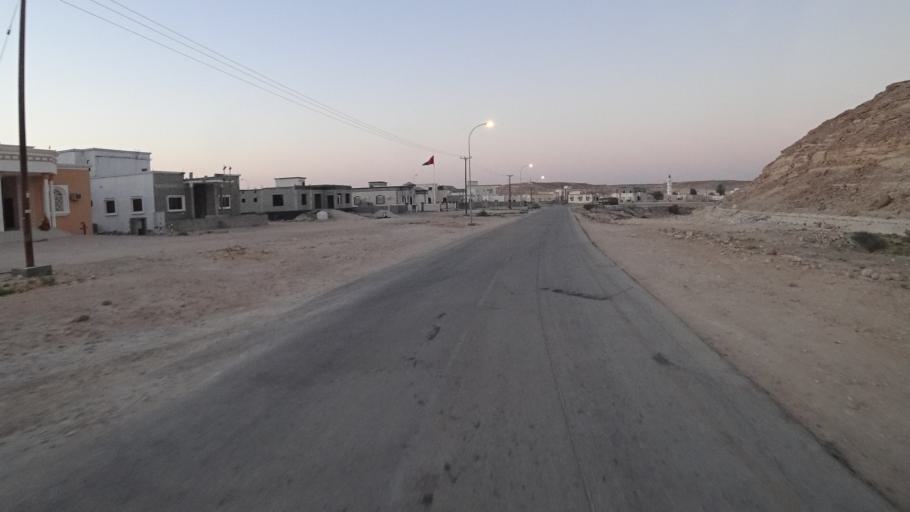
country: OM
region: Zufar
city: Salalah
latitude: 17.4835
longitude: 53.3491
